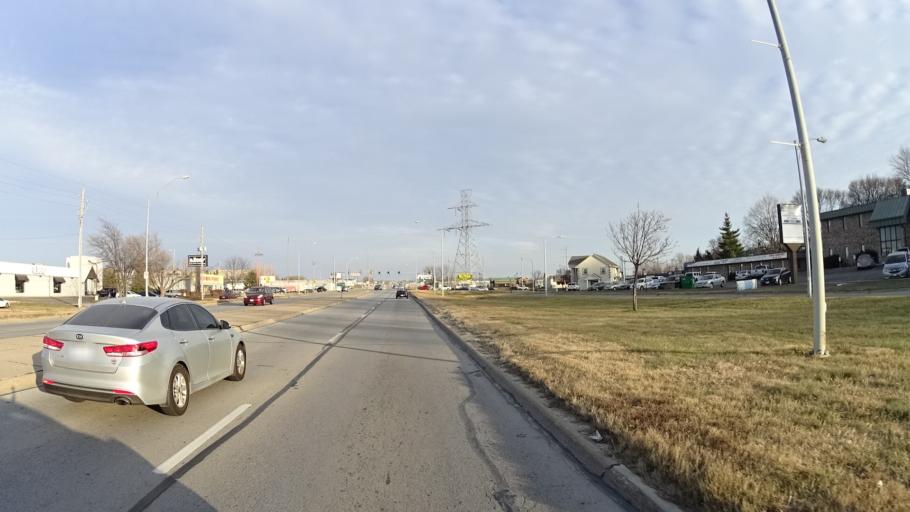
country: US
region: Nebraska
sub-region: Douglas County
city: Ralston
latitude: 41.2125
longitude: -96.0360
